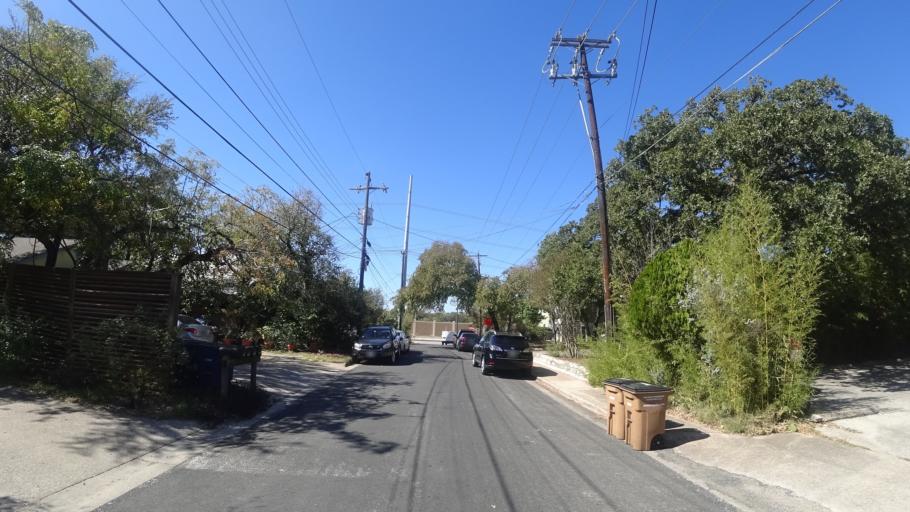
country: US
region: Texas
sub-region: Travis County
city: Austin
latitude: 30.2832
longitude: -97.7638
